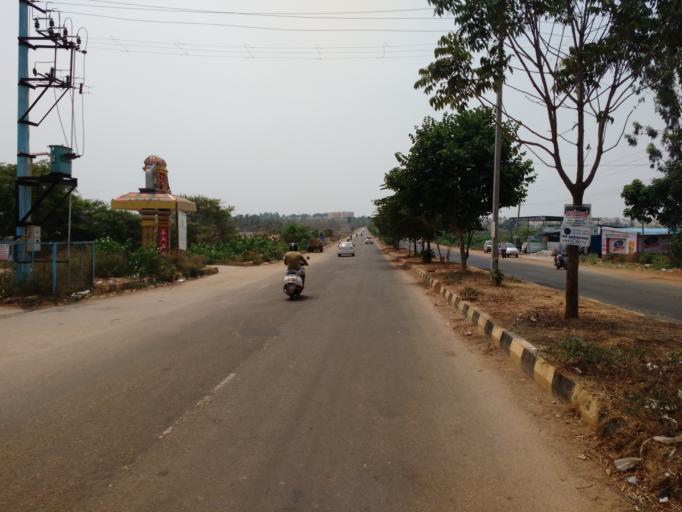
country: IN
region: Karnataka
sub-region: Hassan
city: Hassan
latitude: 13.0197
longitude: 76.1145
